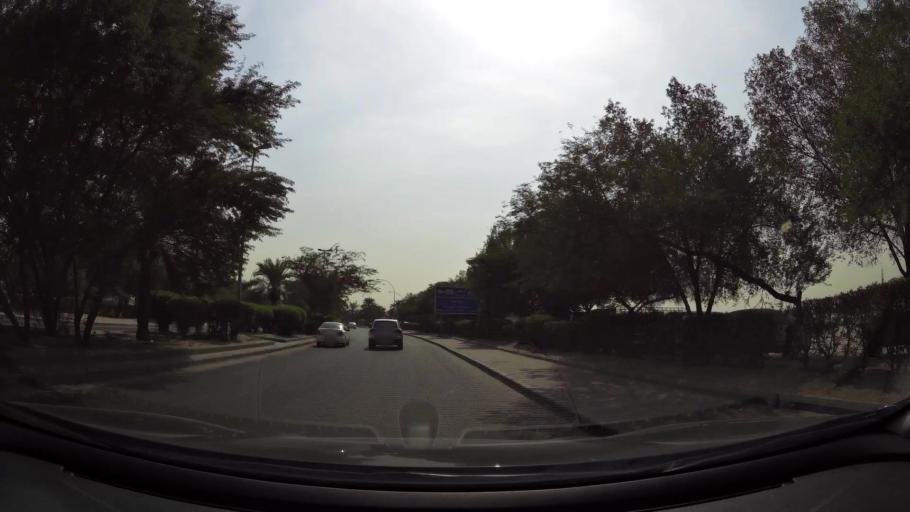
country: KW
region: Al Farwaniyah
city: Al Farwaniyah
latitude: 29.2540
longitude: 47.9463
